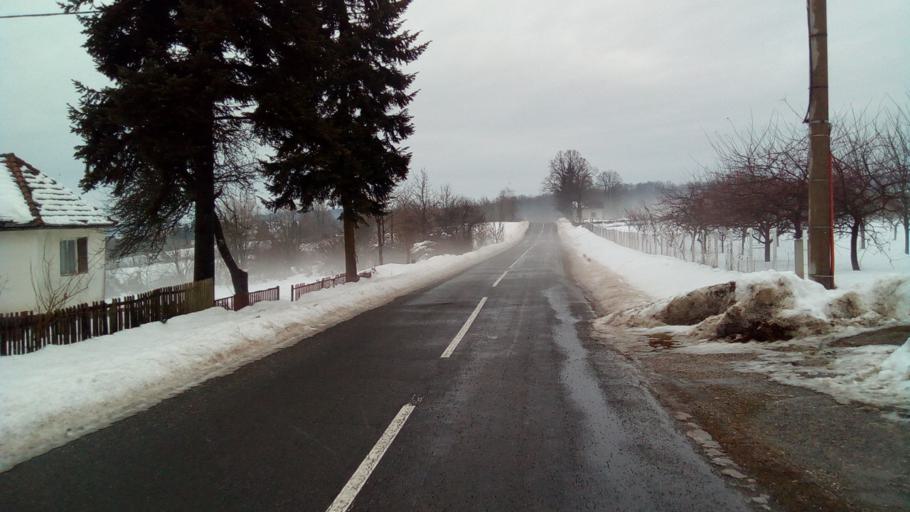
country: HR
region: Sisacko-Moslavacka
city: Petrinja
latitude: 45.3545
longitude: 16.2510
